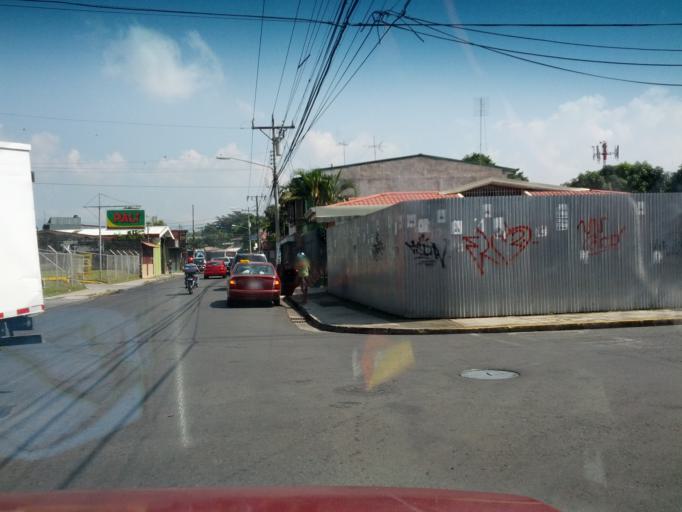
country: CR
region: Alajuela
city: Alajuela
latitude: 10.0212
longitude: -84.2085
